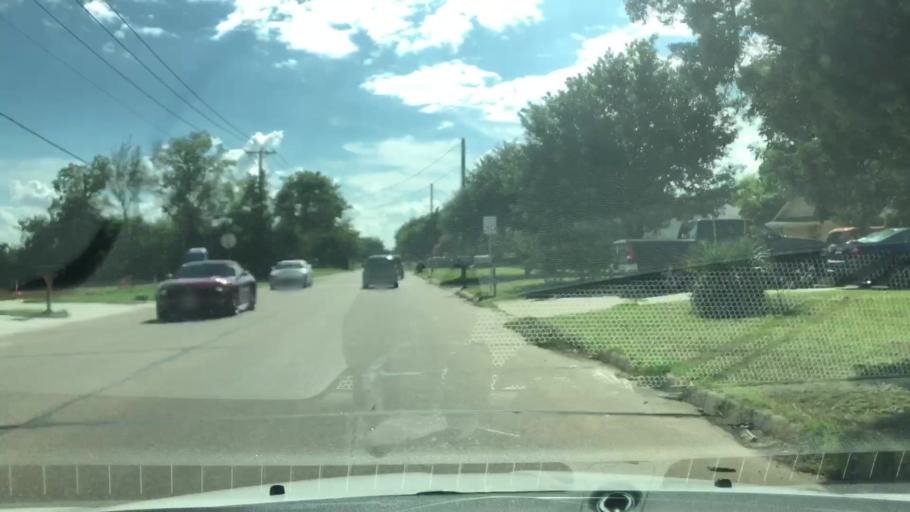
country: US
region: Texas
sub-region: Ellis County
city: Ennis
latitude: 32.3511
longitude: -96.6430
